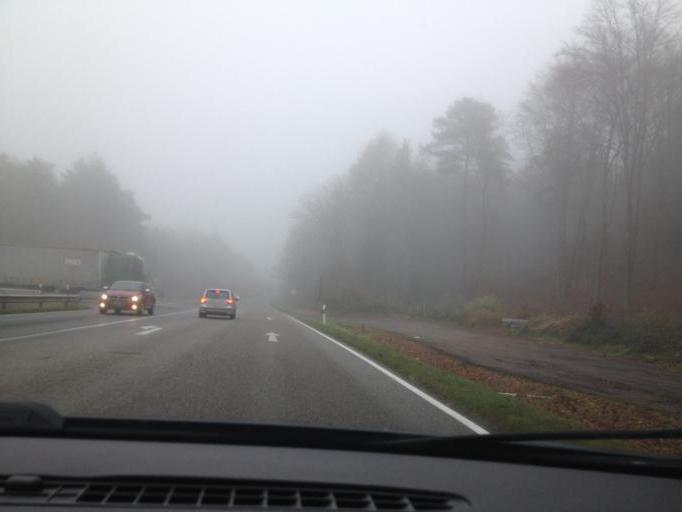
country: DE
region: Rheinland-Pfalz
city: Schwedelbach
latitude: 49.4775
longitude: 7.6035
